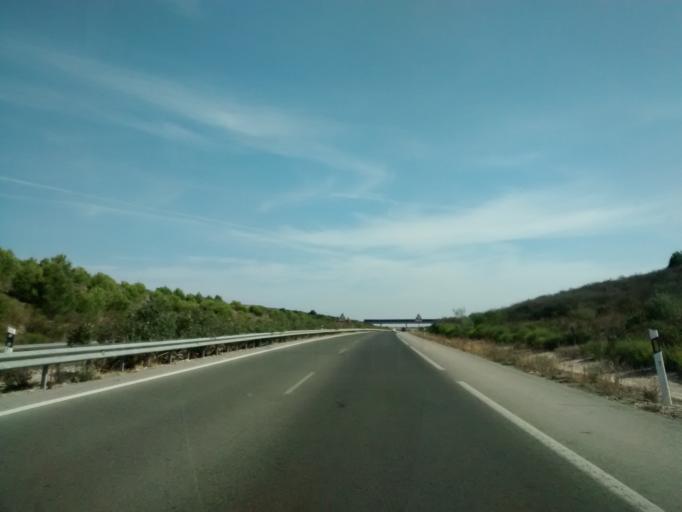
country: ES
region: Andalusia
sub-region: Provincia de Cadiz
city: Conil de la Frontera
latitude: 36.3242
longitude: -6.0558
